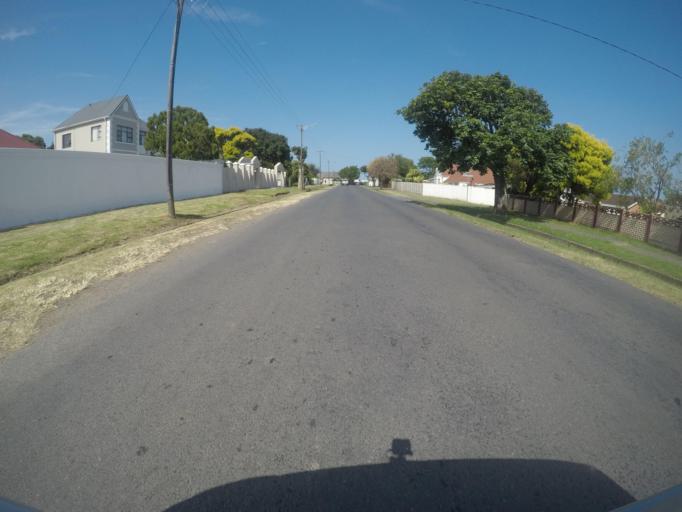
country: ZA
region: Eastern Cape
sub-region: Buffalo City Metropolitan Municipality
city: East London
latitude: -32.9787
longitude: 27.8875
